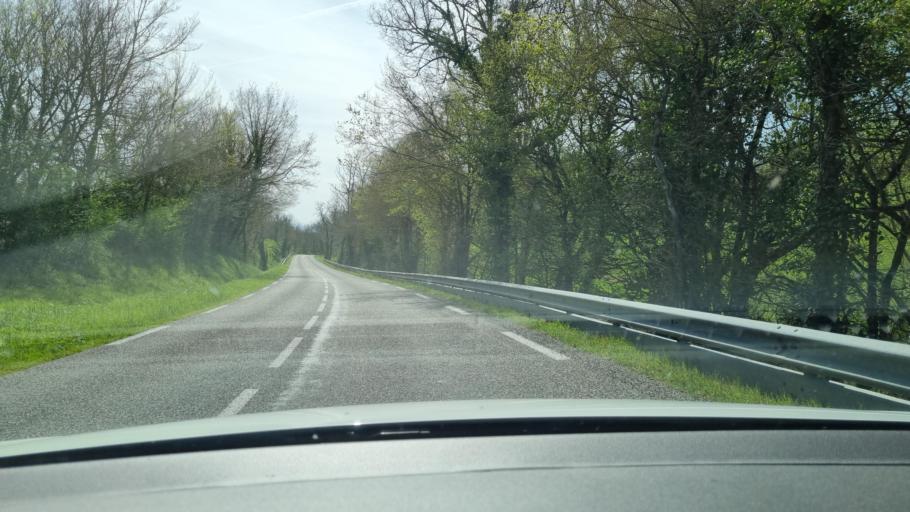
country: FR
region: Midi-Pyrenees
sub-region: Departement du Gers
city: Samatan
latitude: 43.4933
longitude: 0.9983
